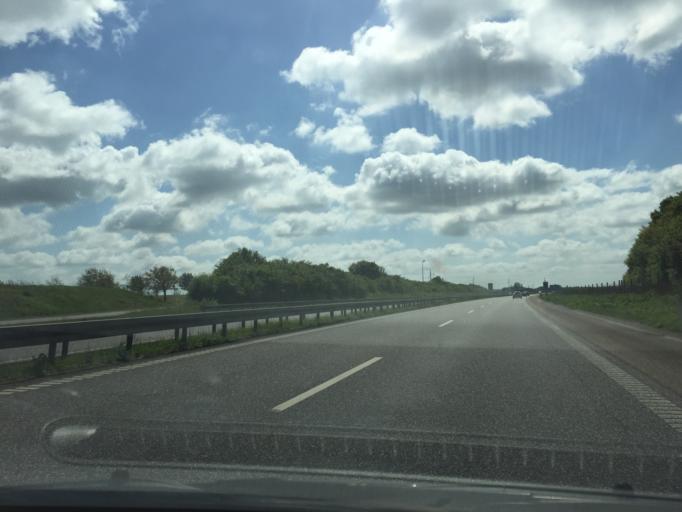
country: DK
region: Zealand
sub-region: Guldborgsund Kommune
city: Sundby
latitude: 54.8425
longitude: 11.8226
